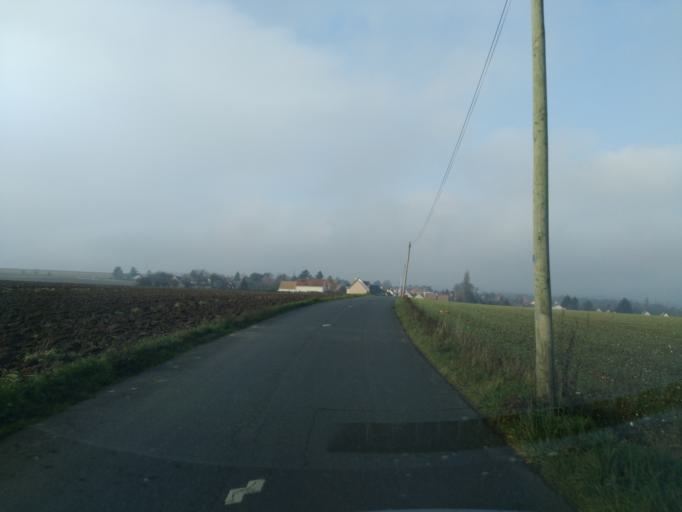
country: FR
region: Ile-de-France
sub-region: Departement des Yvelines
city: Saint-Germain-de-la-Grange
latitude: 48.8318
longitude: 1.9079
